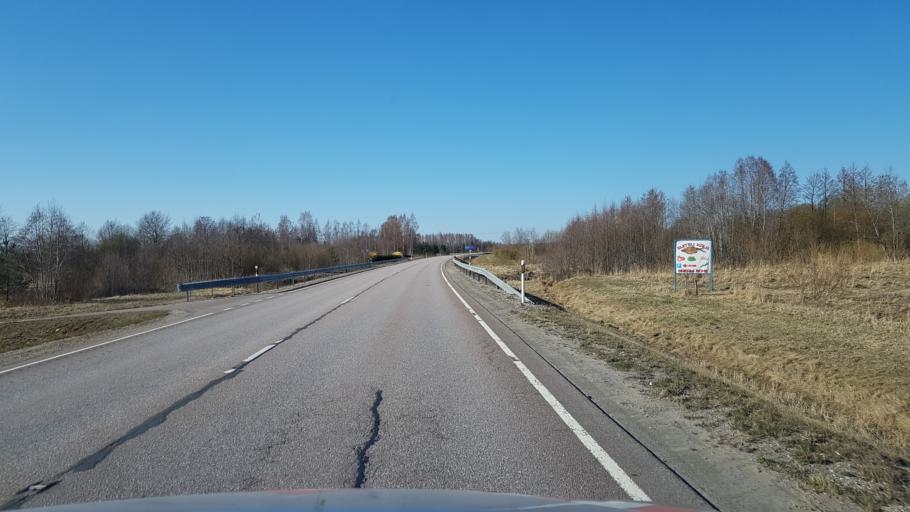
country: EE
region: Jogevamaa
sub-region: Mustvee linn
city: Mustvee
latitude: 58.8071
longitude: 26.9374
